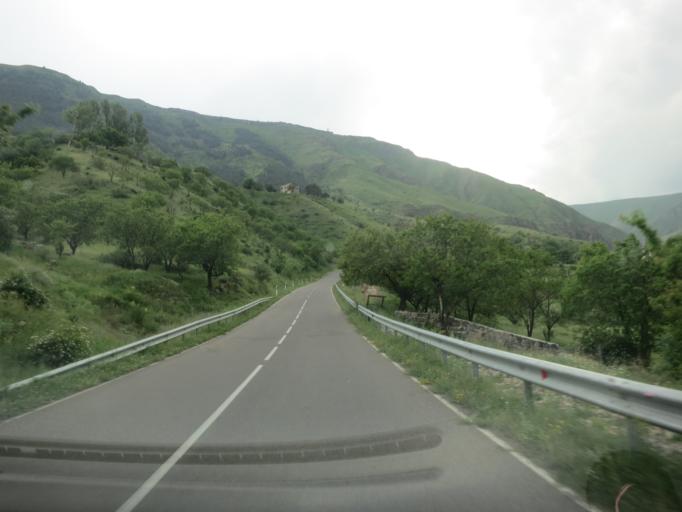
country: TR
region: Ardahan
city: Kurtkale
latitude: 41.3782
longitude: 43.2859
